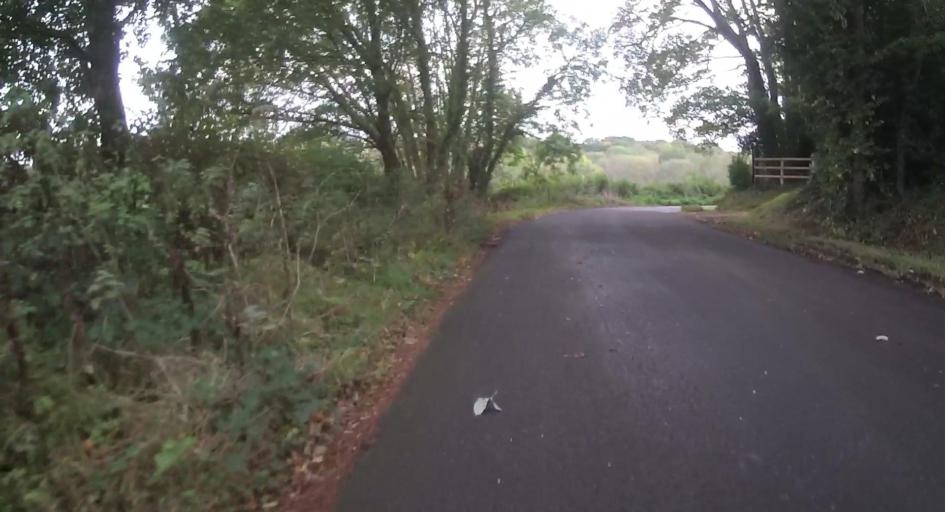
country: GB
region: England
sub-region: West Berkshire
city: Thatcham
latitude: 51.4033
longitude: -1.1847
